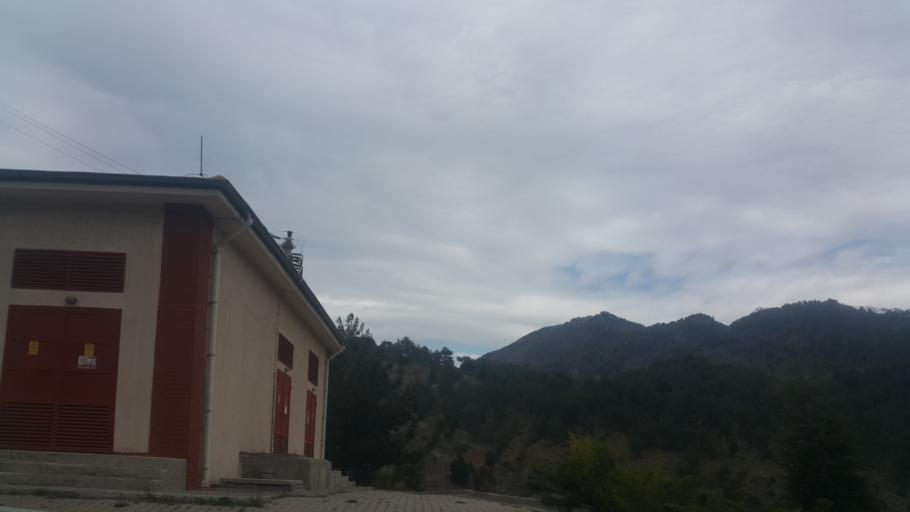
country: TR
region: Nigde
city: Ciftehan
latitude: 37.5213
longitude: 34.8177
